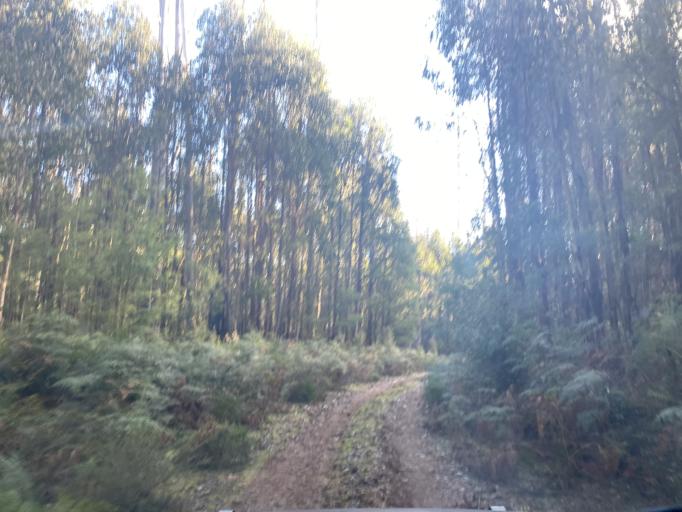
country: AU
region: Victoria
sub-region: Yarra Ranges
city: Healesville
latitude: -37.4741
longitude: 145.5762
